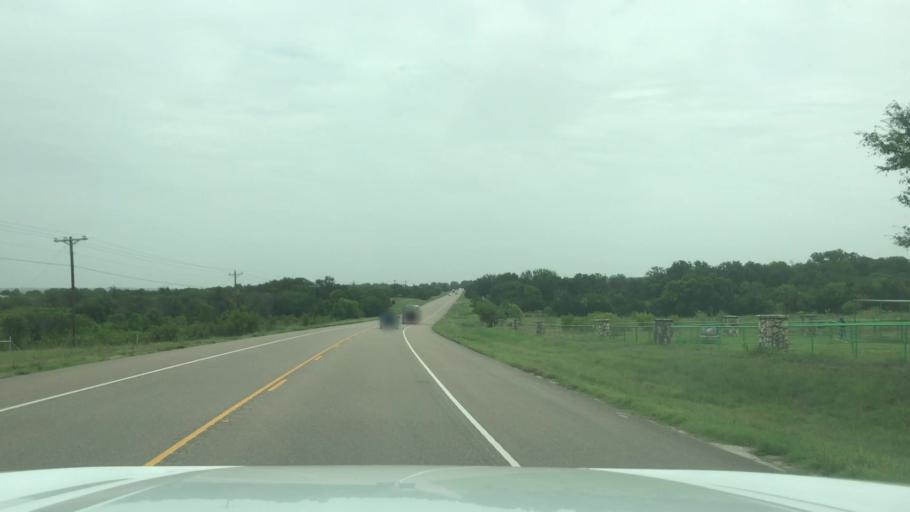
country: US
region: Texas
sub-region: Bosque County
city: Meridian
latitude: 31.9432
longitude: -97.7165
